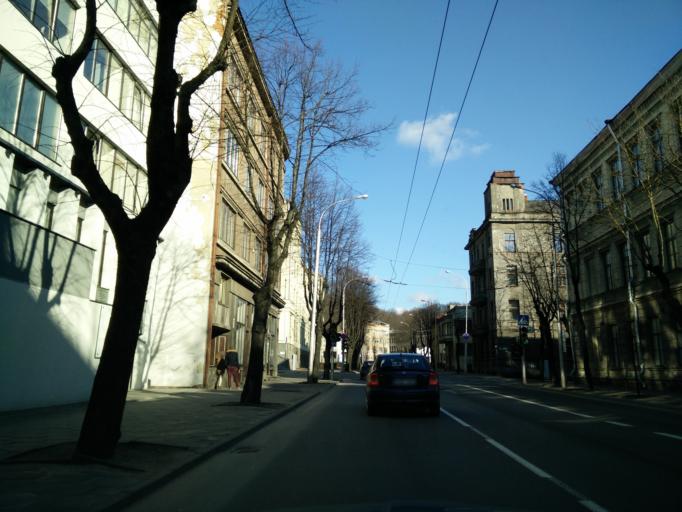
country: LT
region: Kauno apskritis
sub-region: Kaunas
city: Kaunas
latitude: 54.8988
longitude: 23.9208
